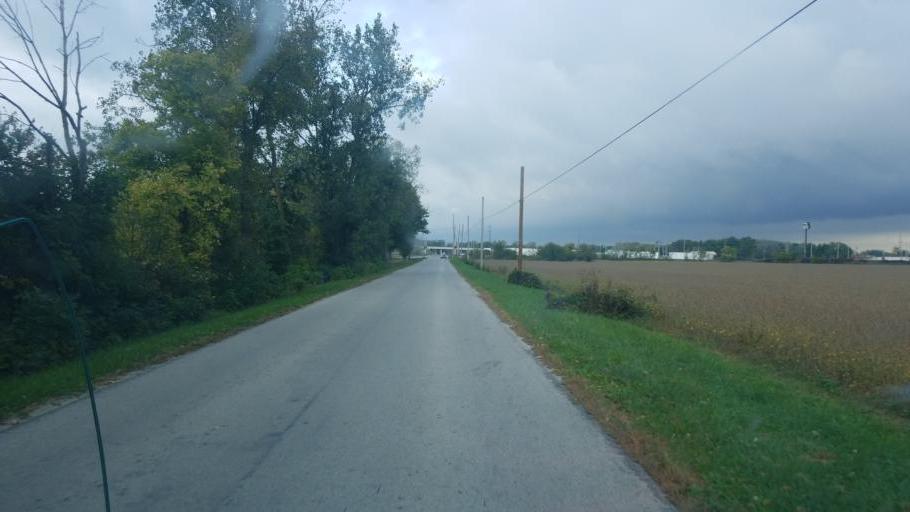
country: US
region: Ohio
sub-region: Wood County
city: North Baltimore
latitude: 41.1822
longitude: -83.6422
